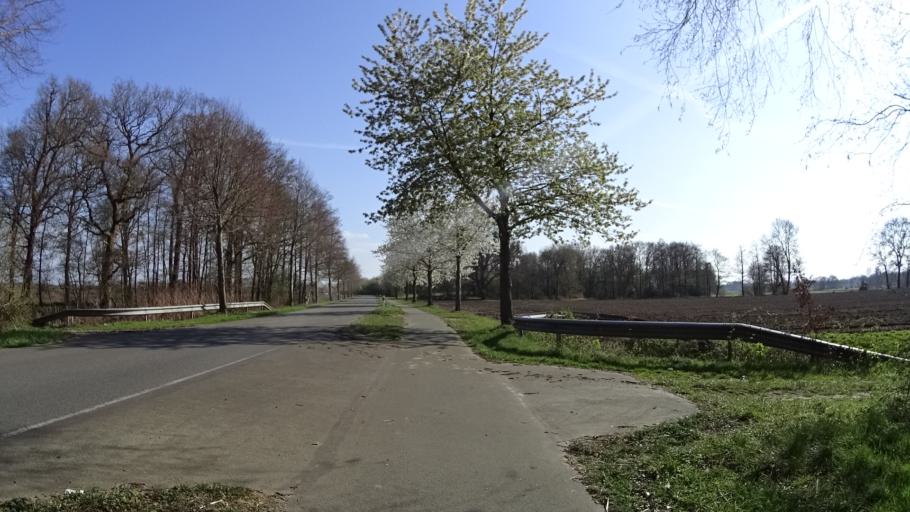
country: DE
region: Lower Saxony
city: Dorpen
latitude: 52.9459
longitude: 7.3159
